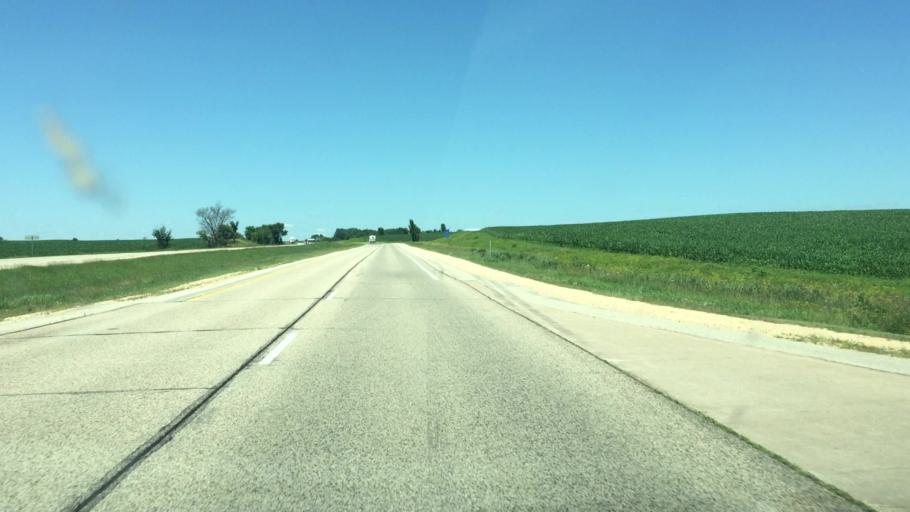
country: US
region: Iowa
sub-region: Jackson County
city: Maquoketa
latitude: 42.2071
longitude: -90.6716
